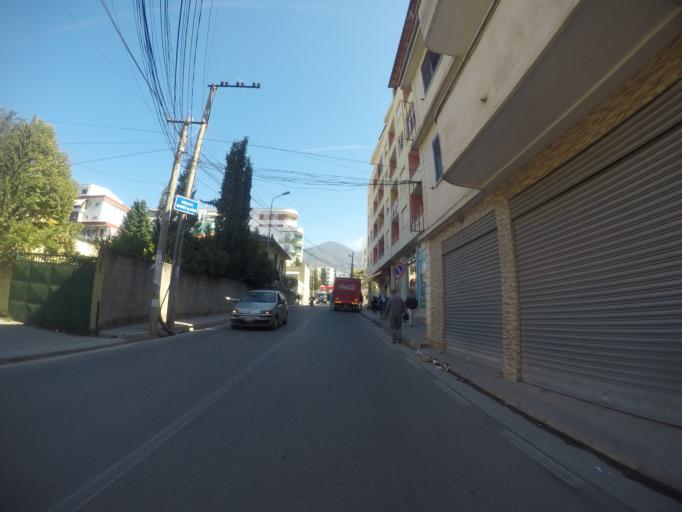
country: AL
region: Tirane
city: Tirana
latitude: 41.3478
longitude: 19.8568
